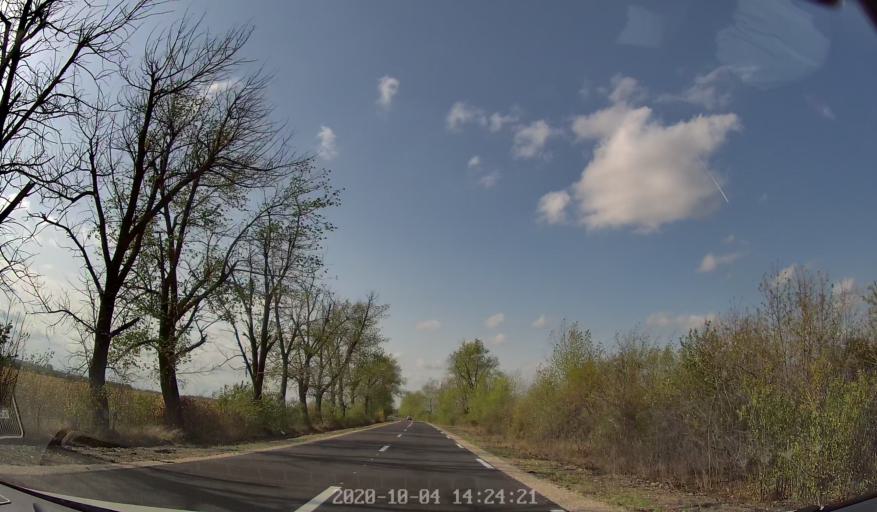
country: MD
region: Rezina
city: Saharna
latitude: 47.6141
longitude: 28.9189
